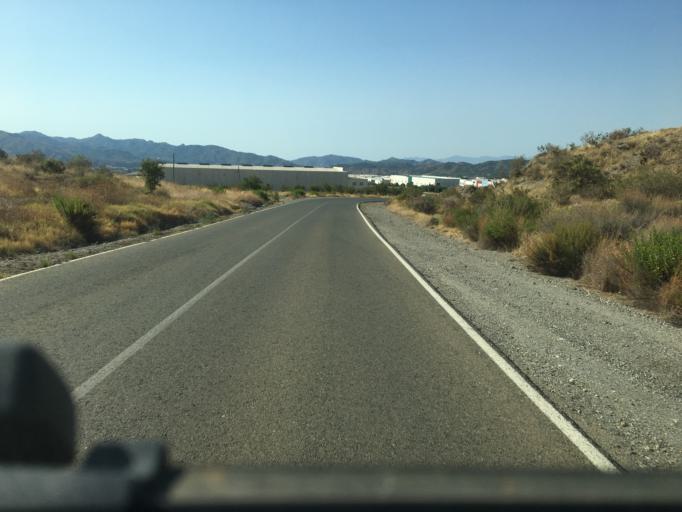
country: ES
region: Andalusia
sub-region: Provincia de Almeria
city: Huercal-Overa
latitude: 37.4226
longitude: -1.9697
